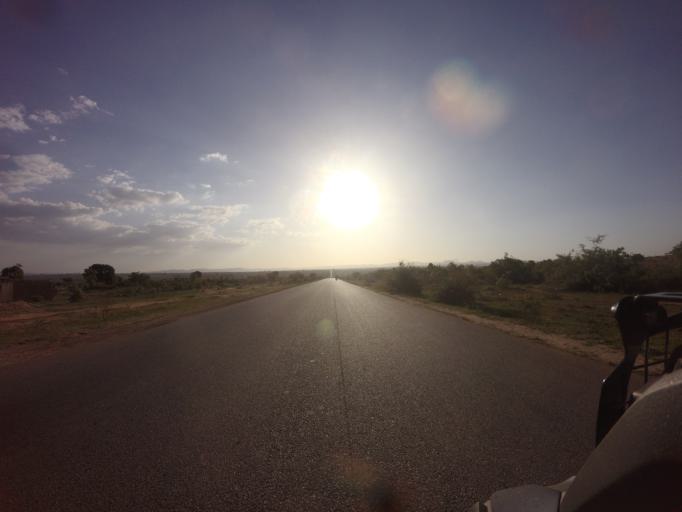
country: AO
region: Huila
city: Lubango
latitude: -14.7929
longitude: 13.6979
